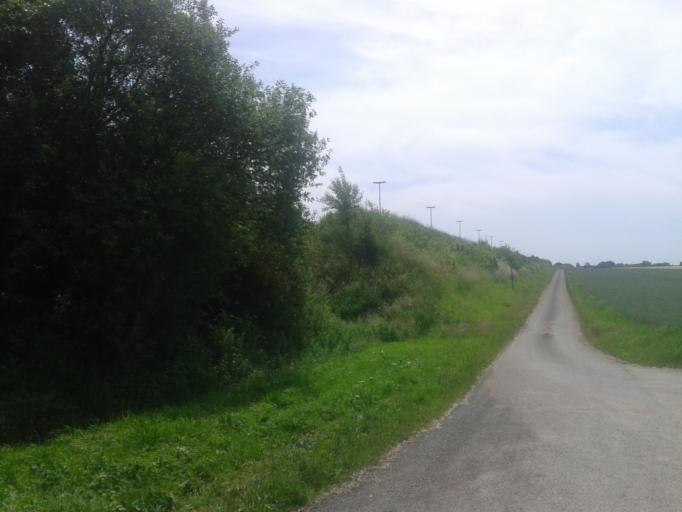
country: BE
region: Wallonia
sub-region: Province de Liege
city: Verlaine
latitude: 50.6028
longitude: 5.3362
